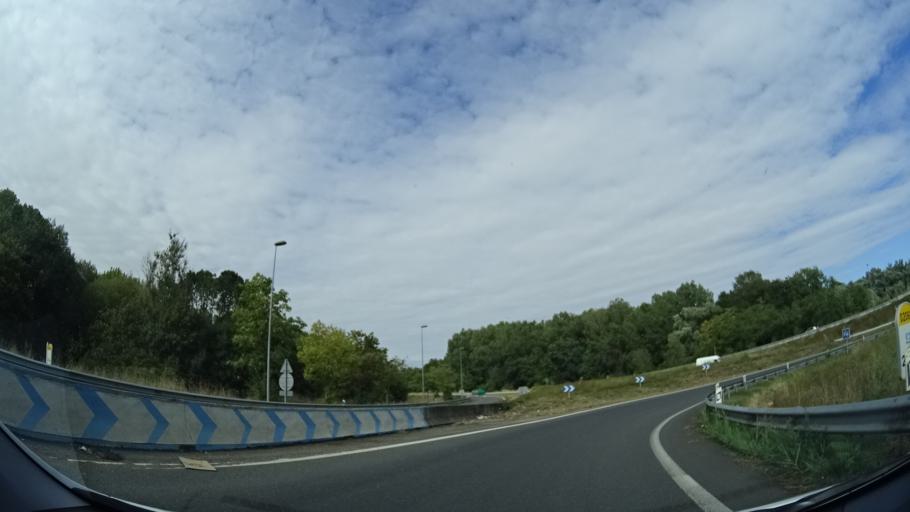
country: FR
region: Centre
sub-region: Departement du Loiret
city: Montargis
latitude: 47.9842
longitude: 2.7414
